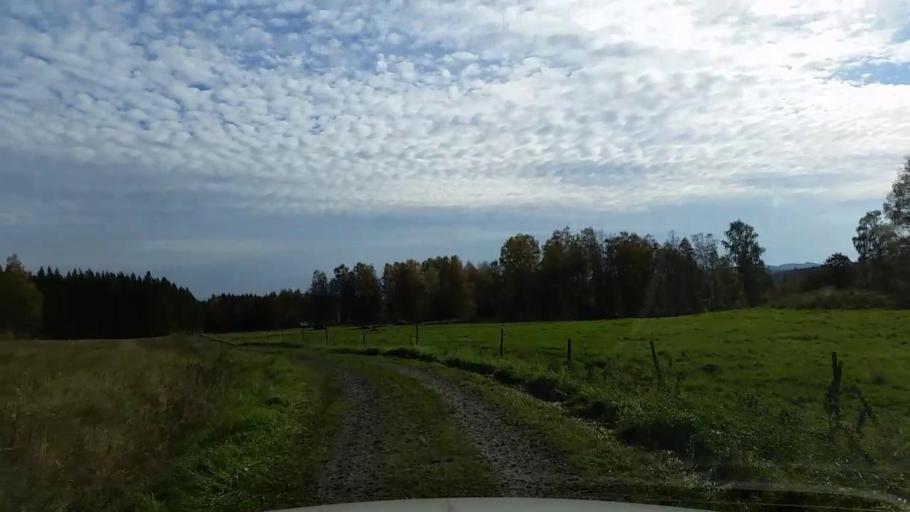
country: SE
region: Gaevleborg
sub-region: Ljusdals Kommun
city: Jaervsoe
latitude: 61.7832
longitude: 16.1665
